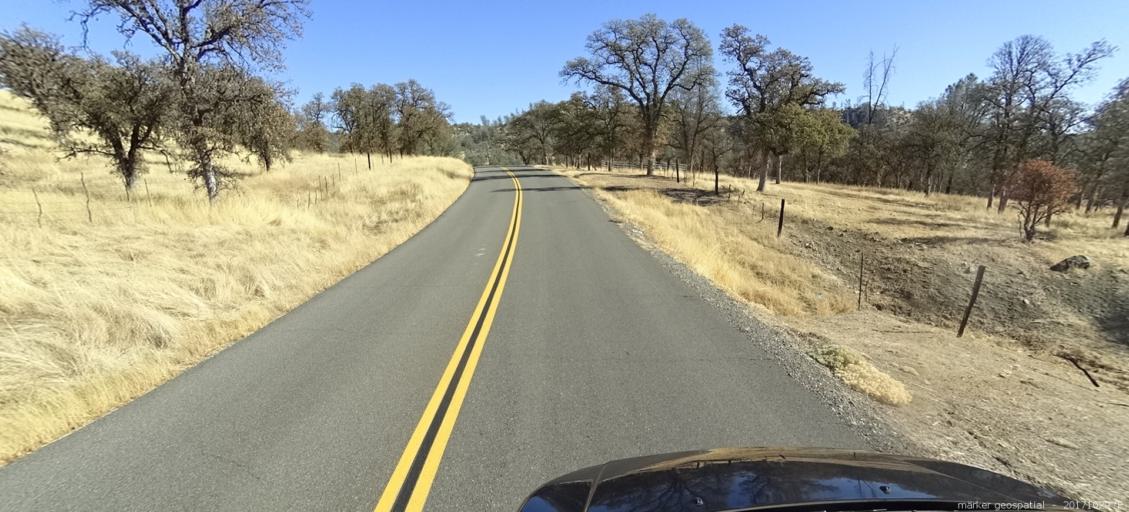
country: US
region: California
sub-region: Shasta County
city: Shasta
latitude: 40.4296
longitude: -122.7166
